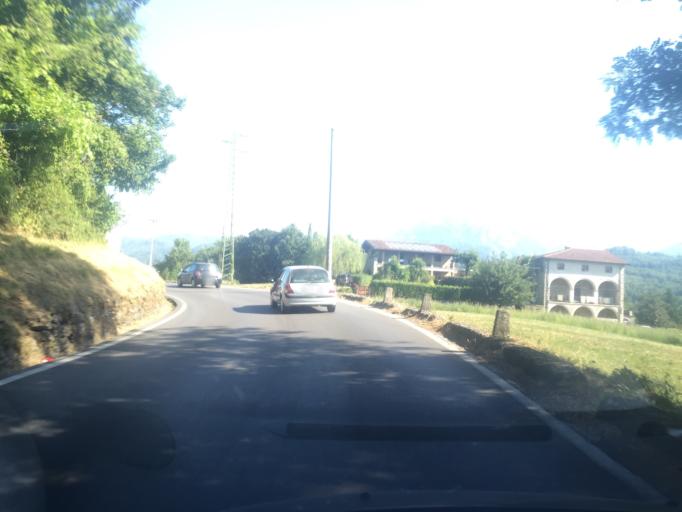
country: IT
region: Tuscany
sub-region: Provincia di Lucca
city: Pieve Fosciana
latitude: 44.1294
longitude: 10.3774
